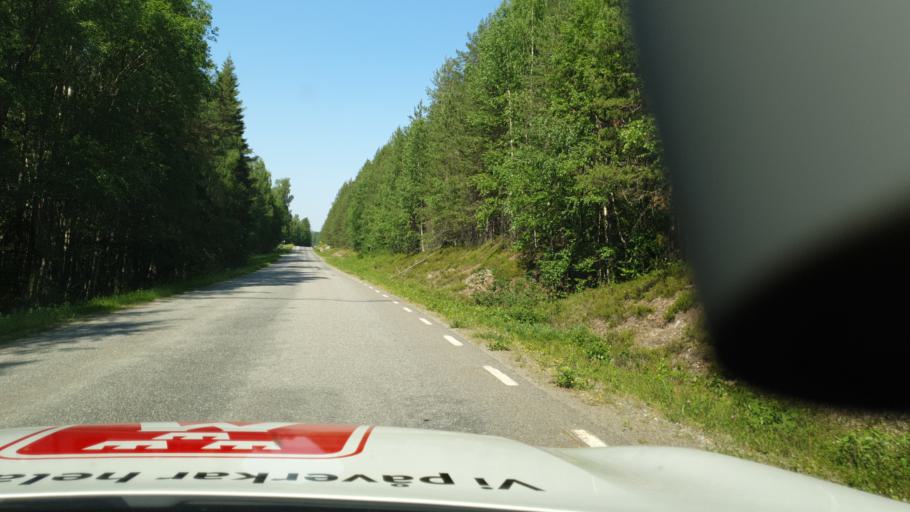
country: SE
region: Vaesterbotten
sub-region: Skelleftea Kommun
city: Langsele
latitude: 64.9604
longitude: 19.8988
